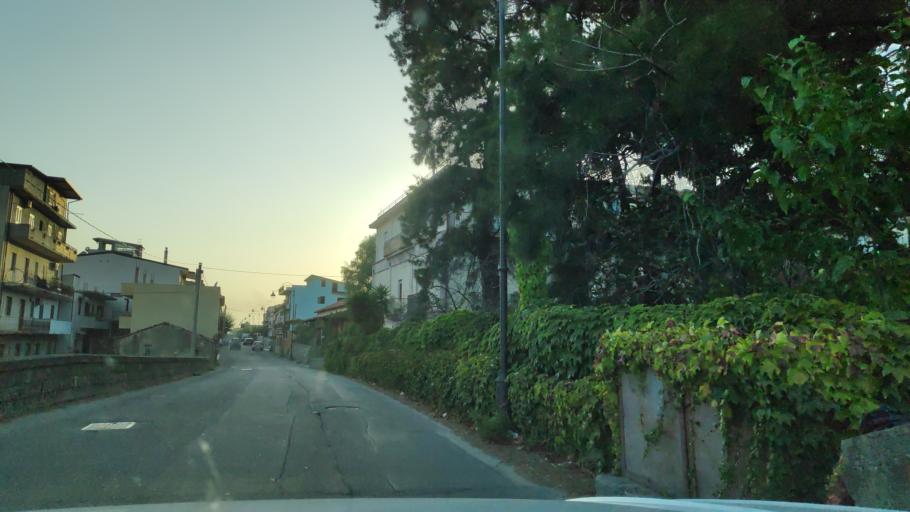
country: IT
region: Calabria
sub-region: Provincia di Reggio Calabria
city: Bova Marina
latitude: 37.9293
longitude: 15.9091
